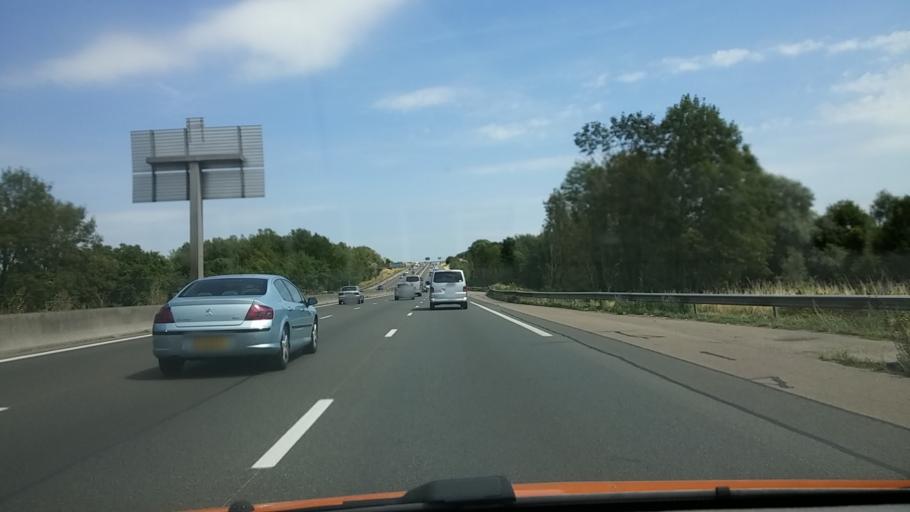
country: FR
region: Ile-de-France
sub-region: Departement de Seine-et-Marne
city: Collegien
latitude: 48.8311
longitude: 2.6855
